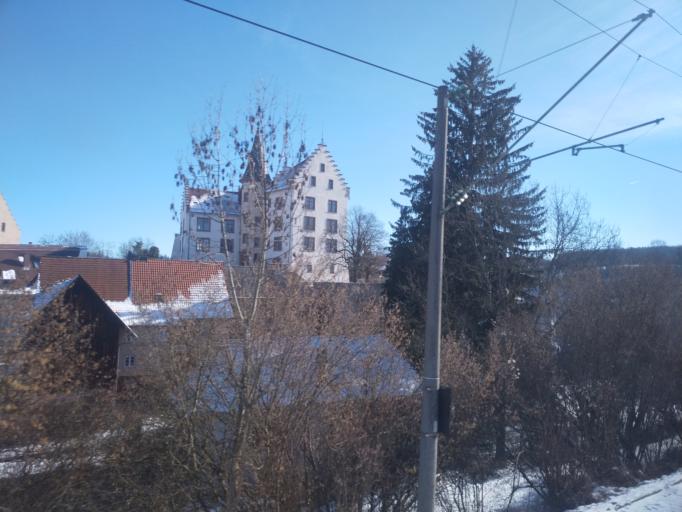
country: DE
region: Baden-Wuerttemberg
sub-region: Freiburg Region
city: Engen
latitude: 47.8501
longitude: 8.7693
